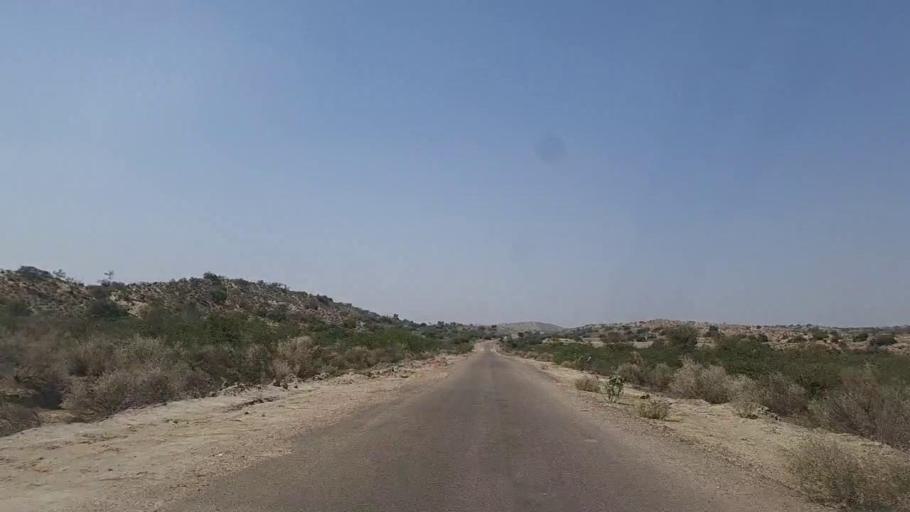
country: PK
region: Sindh
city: Diplo
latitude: 24.5474
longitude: 69.4231
